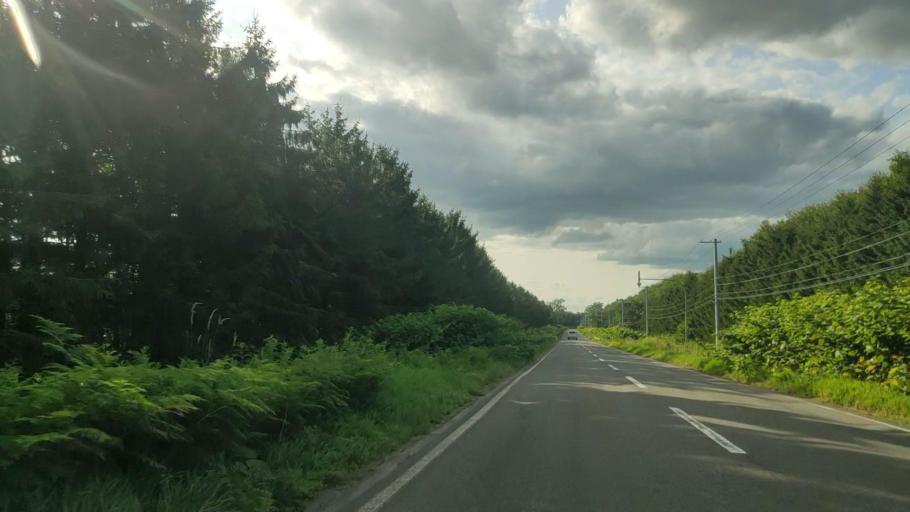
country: JP
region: Hokkaido
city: Makubetsu
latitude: 44.9021
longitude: 141.9091
